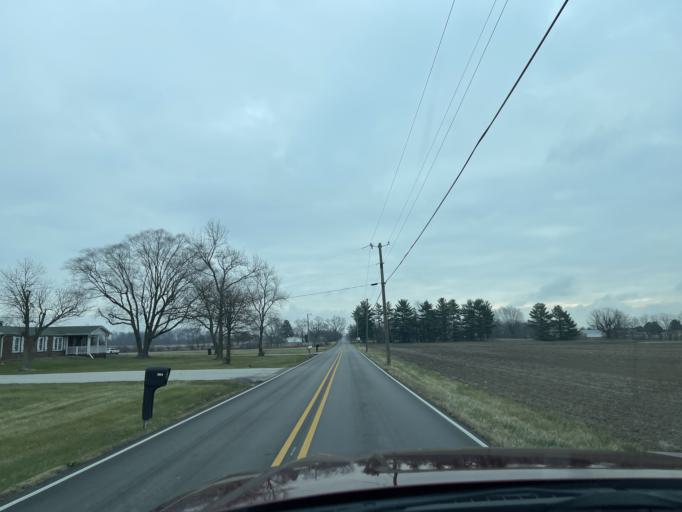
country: US
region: Indiana
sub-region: Boone County
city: Dale
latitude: 39.9456
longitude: -86.3960
